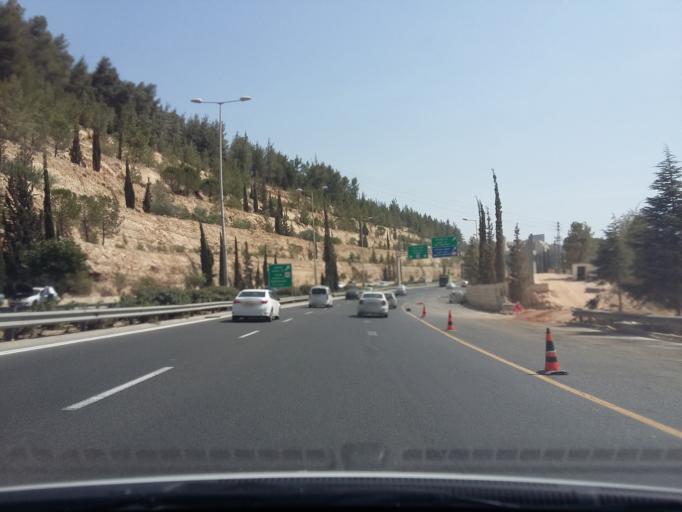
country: IL
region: Jerusalem
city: West Jerusalem
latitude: 31.8131
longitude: 35.2119
